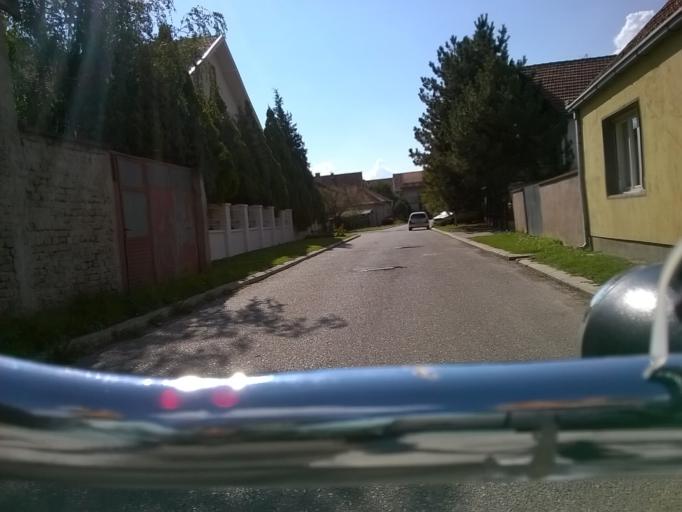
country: RS
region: Autonomna Pokrajina Vojvodina
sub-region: Juznobanatski Okrug
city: Pancevo
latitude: 44.8800
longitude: 20.6409
